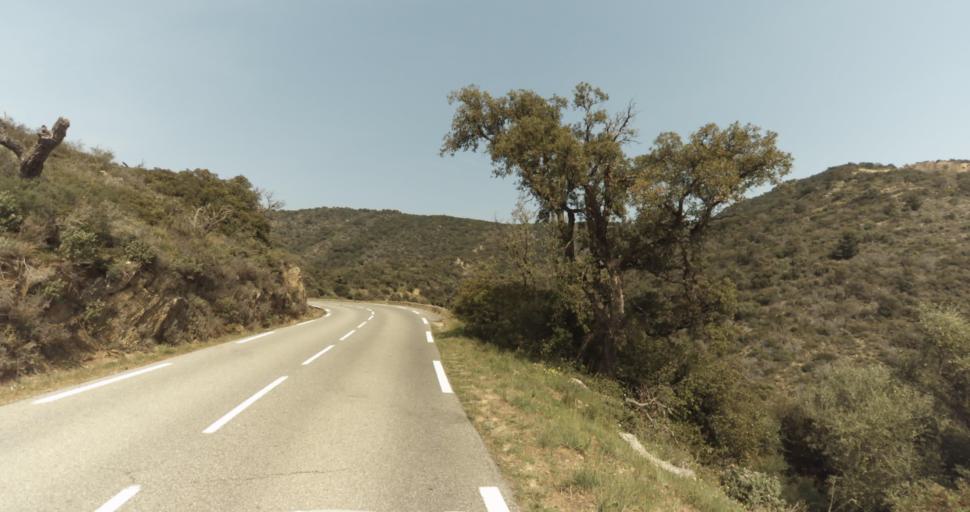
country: FR
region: Provence-Alpes-Cote d'Azur
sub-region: Departement du Var
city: Bormes-les-Mimosas
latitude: 43.1592
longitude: 6.3438
